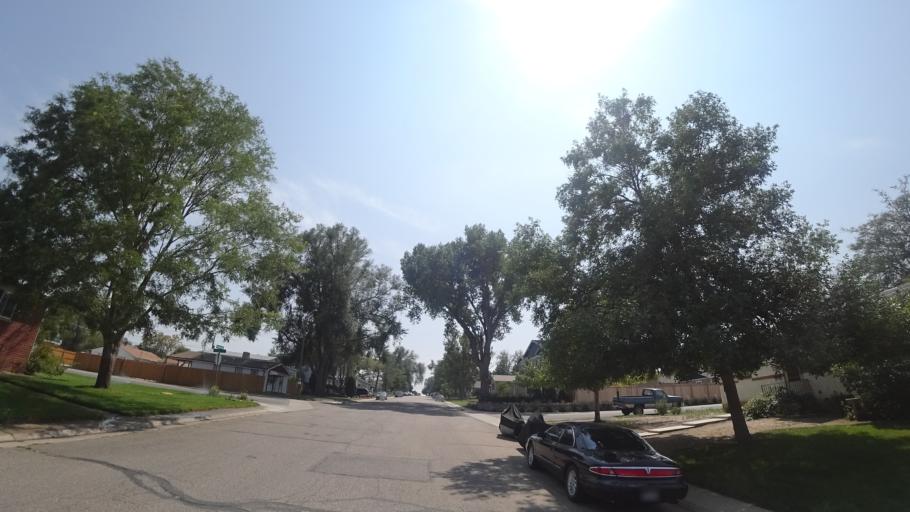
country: US
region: Colorado
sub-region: Arapahoe County
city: Englewood
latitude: 39.6317
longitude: -104.9892
